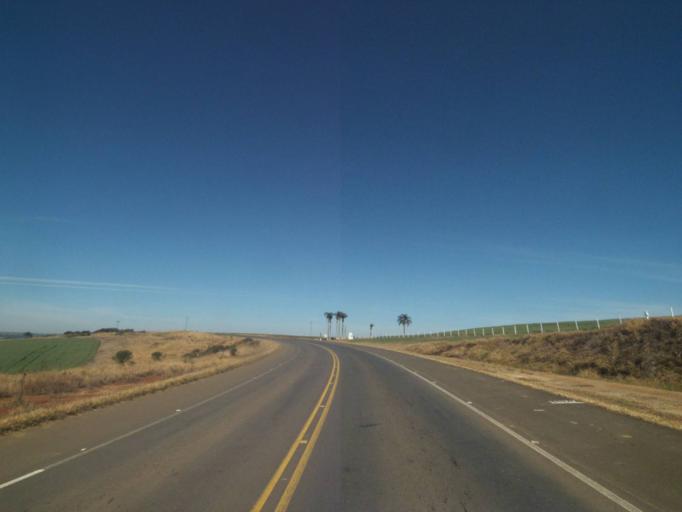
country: BR
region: Parana
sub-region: Tibagi
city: Tibagi
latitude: -24.6344
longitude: -50.4609
